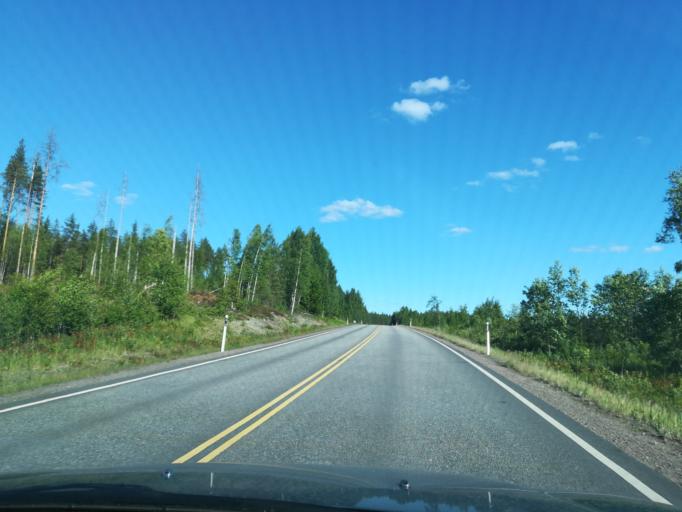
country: FI
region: South Karelia
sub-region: Imatra
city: Ruokolahti
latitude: 61.3919
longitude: 28.6390
